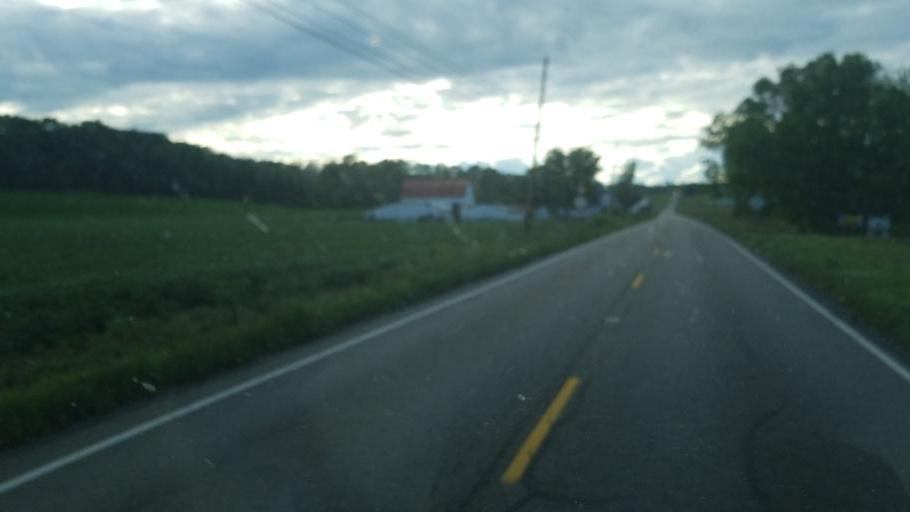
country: US
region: Ohio
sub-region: Knox County
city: Gambier
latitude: 40.4107
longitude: -82.3729
